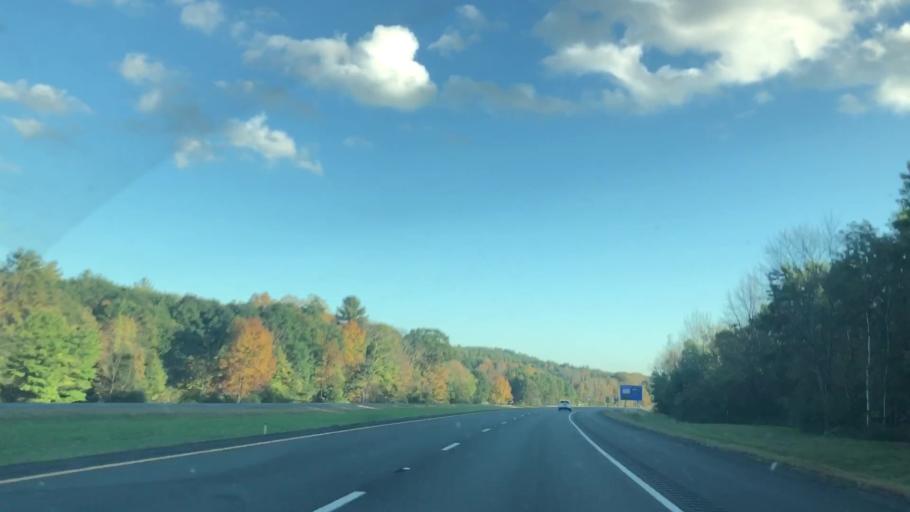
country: US
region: Massachusetts
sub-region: Franklin County
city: Bernardston
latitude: 42.6949
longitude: -72.5469
